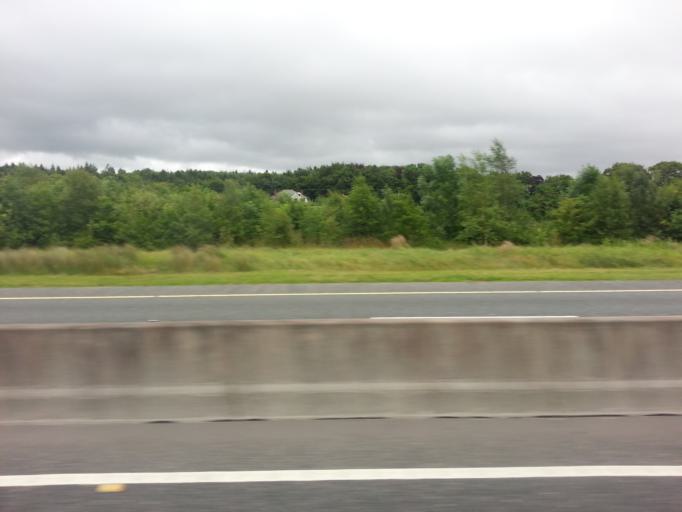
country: IE
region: Leinster
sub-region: Kildare
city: Castledermot
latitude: 52.8510
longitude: -6.8398
